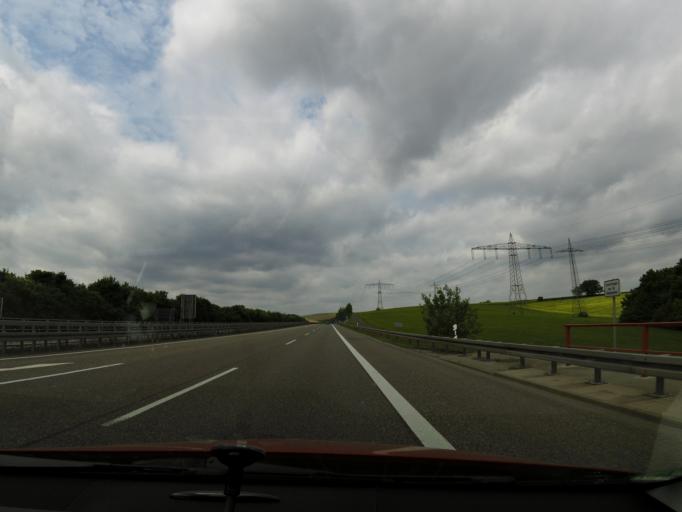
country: DE
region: Thuringia
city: Lauchroden
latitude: 51.0169
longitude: 10.1321
